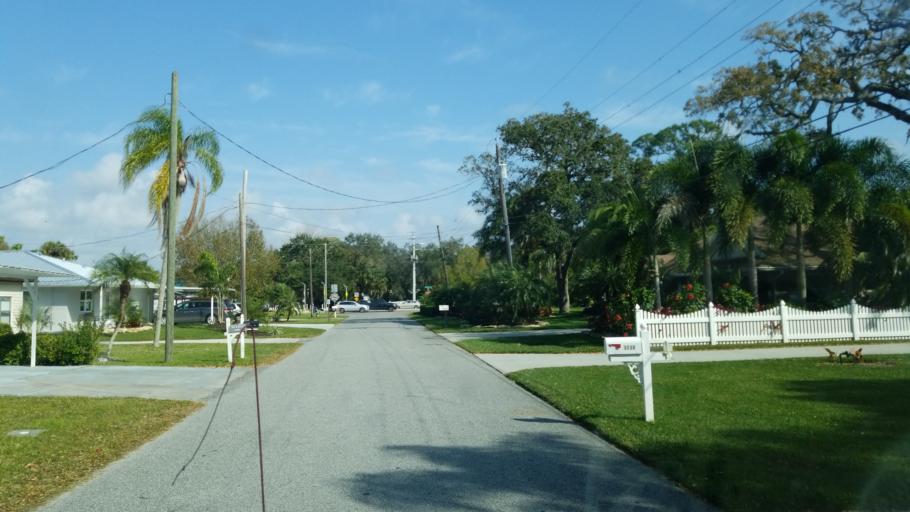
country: US
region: Florida
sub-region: Sarasota County
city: Southgate
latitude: 27.3220
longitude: -82.4976
